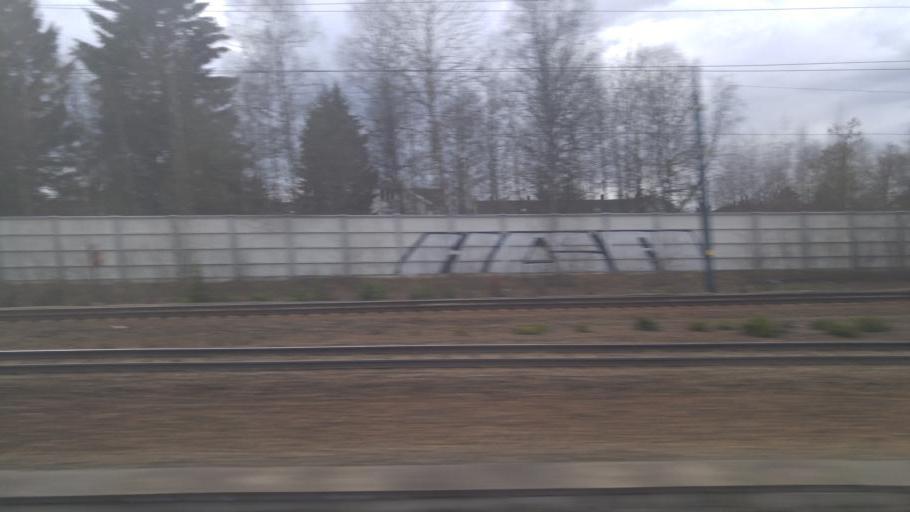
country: NO
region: Akershus
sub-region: Ullensaker
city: Klofta
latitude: 60.0735
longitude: 11.1394
